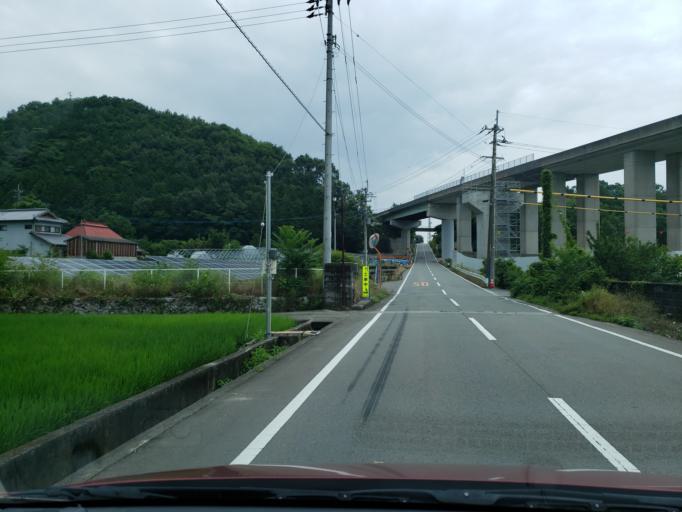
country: JP
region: Tokushima
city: Wakimachi
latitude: 34.1043
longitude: 134.2383
